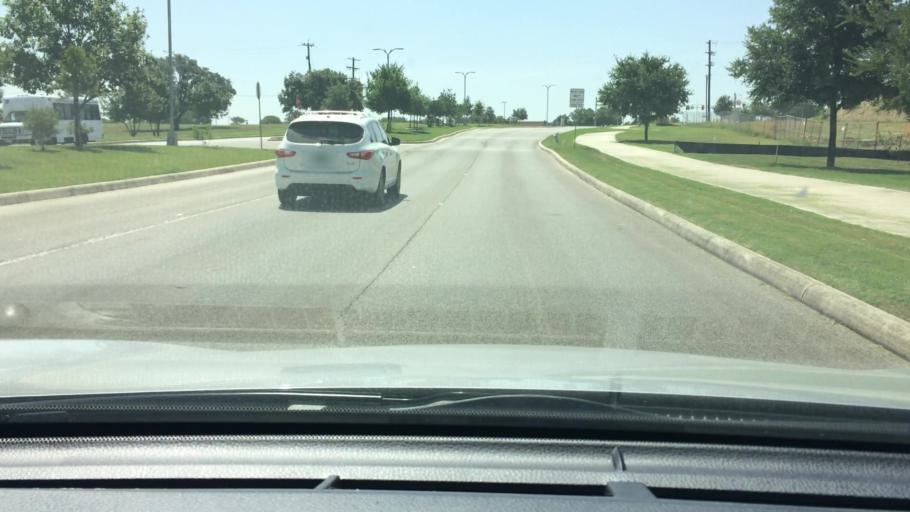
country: US
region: Texas
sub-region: Bexar County
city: San Antonio
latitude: 29.3474
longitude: -98.4465
